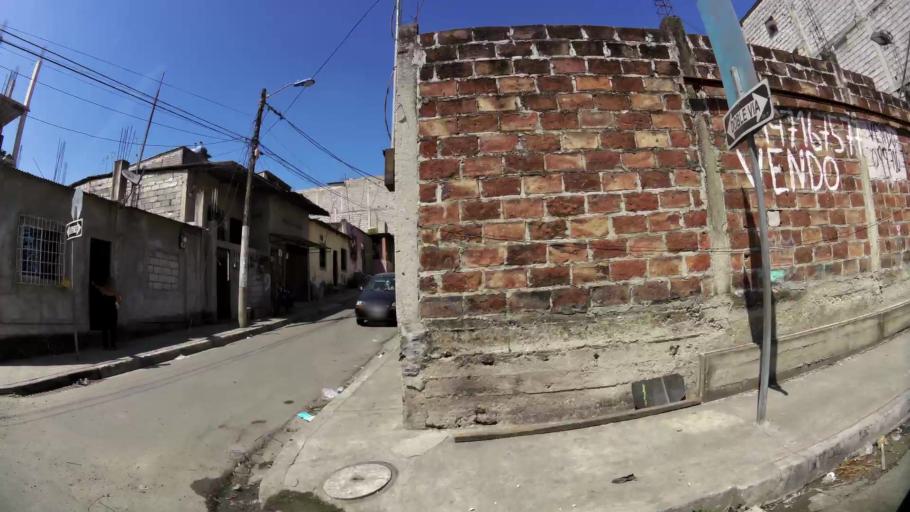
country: EC
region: Guayas
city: Guayaquil
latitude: -2.1286
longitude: -79.9189
